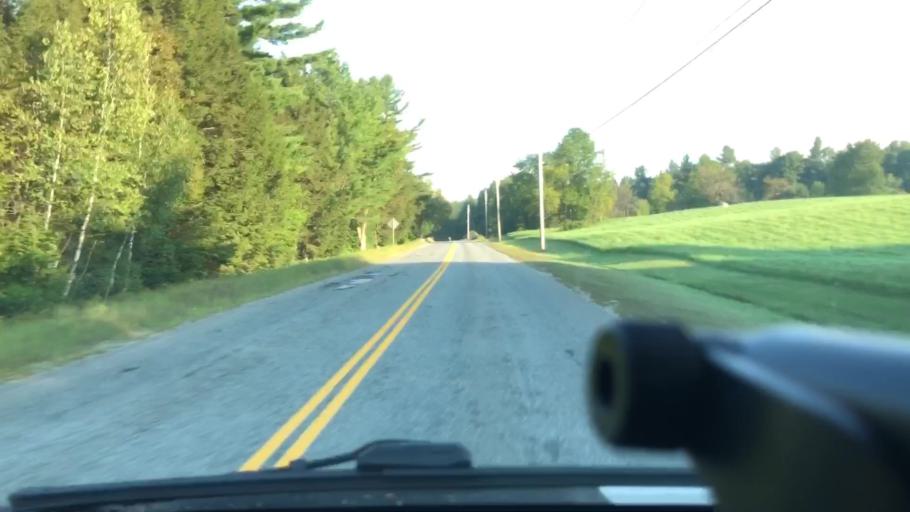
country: US
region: Massachusetts
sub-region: Franklin County
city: Ashfield
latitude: 42.5072
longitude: -72.8827
